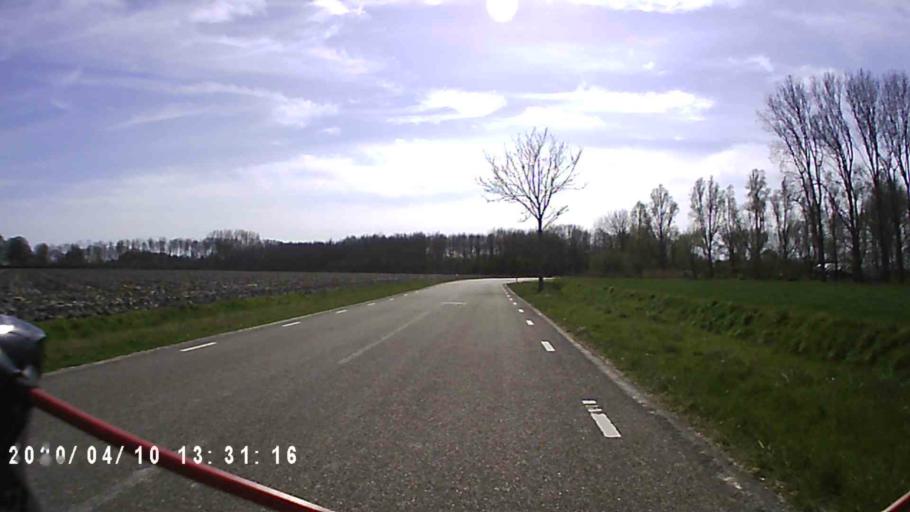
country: NL
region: Groningen
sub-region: Gemeente Zuidhorn
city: Oldehove
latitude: 53.3657
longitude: 6.4190
